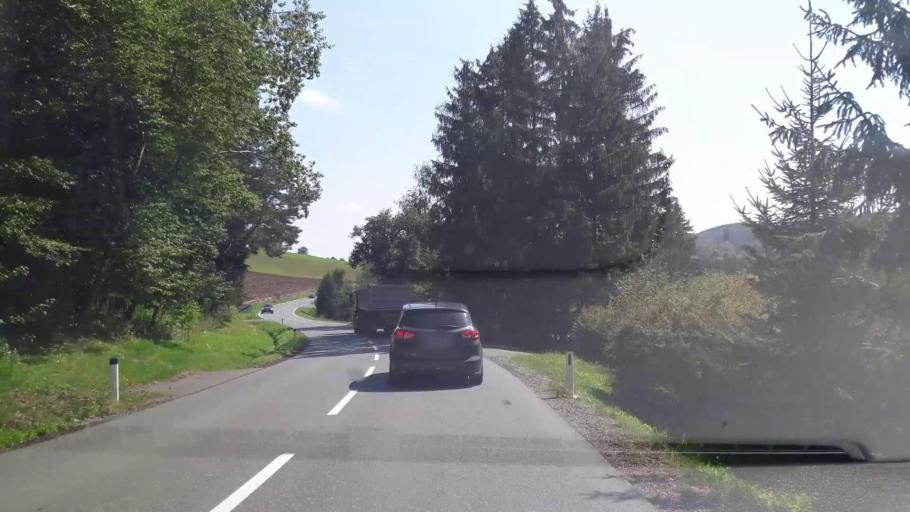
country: AT
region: Styria
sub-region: Politischer Bezirk Hartberg-Fuerstenfeld
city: Stubenberg
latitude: 47.2275
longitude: 15.8109
